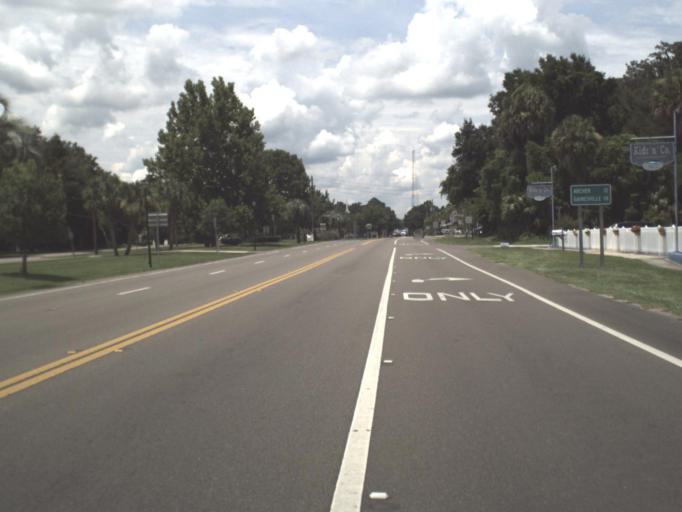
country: US
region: Florida
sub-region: Levy County
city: Williston
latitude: 29.3913
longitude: -82.4481
